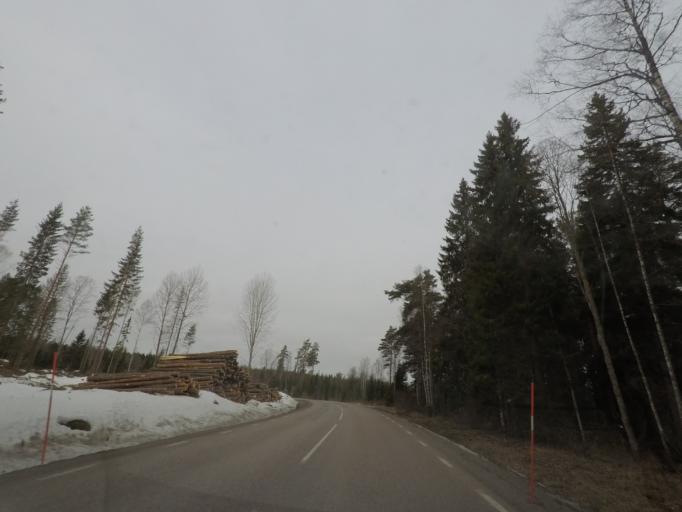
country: SE
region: Vaestmanland
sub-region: Vasteras
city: Skultuna
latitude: 59.7414
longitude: 16.3828
